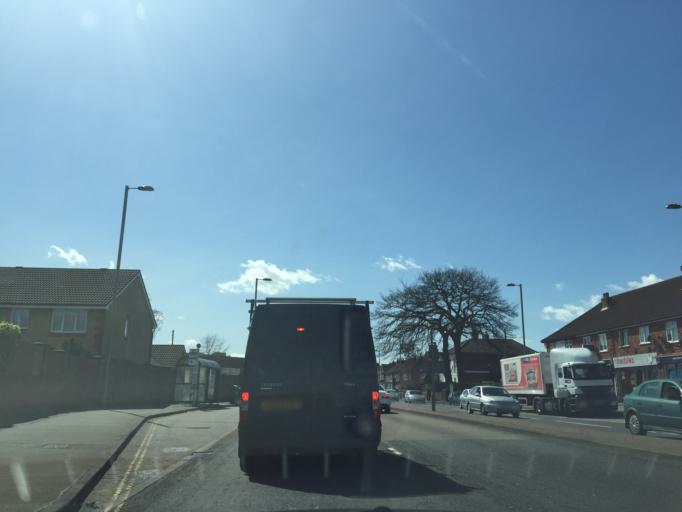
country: GB
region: England
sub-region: Hampshire
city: Fareham
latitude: 50.8466
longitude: -1.1822
